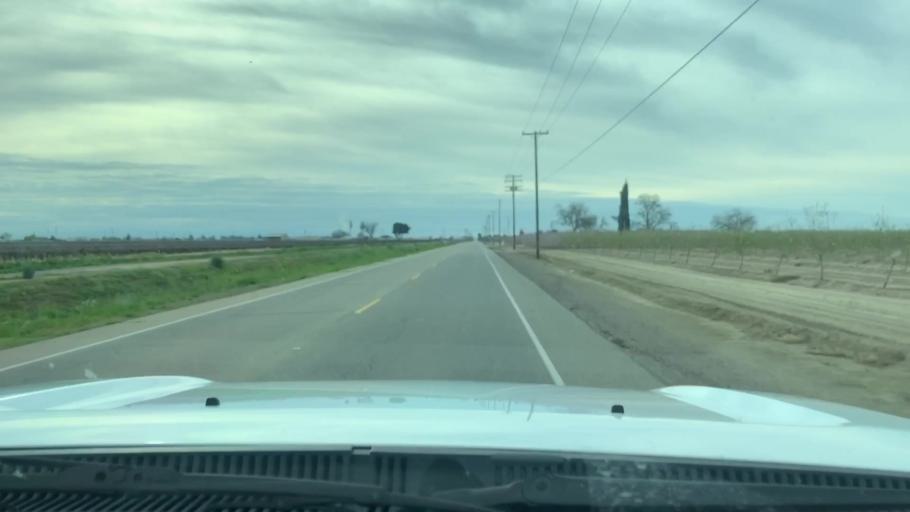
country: US
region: California
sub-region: Fresno County
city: Fowler
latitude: 36.6055
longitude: -119.7105
